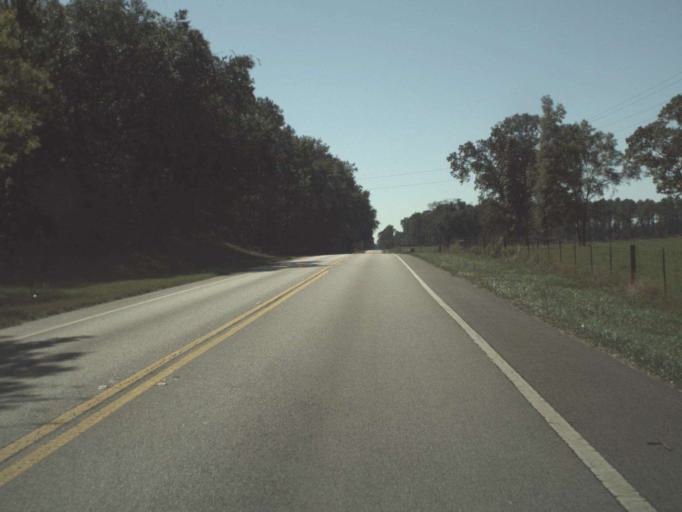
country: US
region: Alabama
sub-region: Geneva County
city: Samson
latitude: 30.9467
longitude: -86.1372
